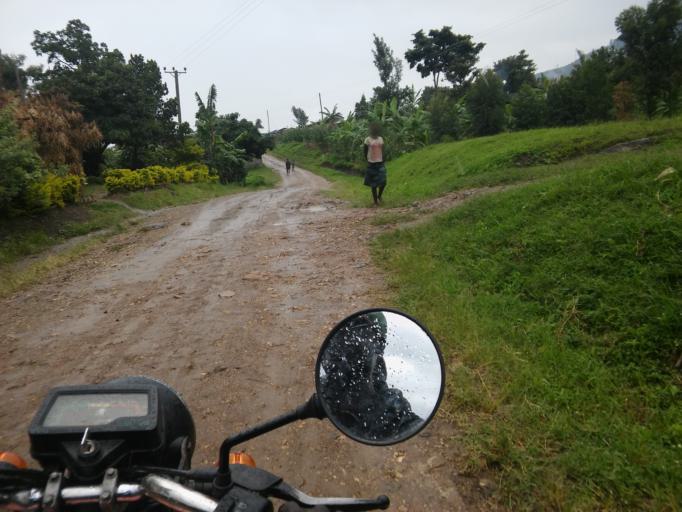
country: UG
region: Eastern Region
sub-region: Bududa District
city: Bududa
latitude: 1.0091
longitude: 34.2362
